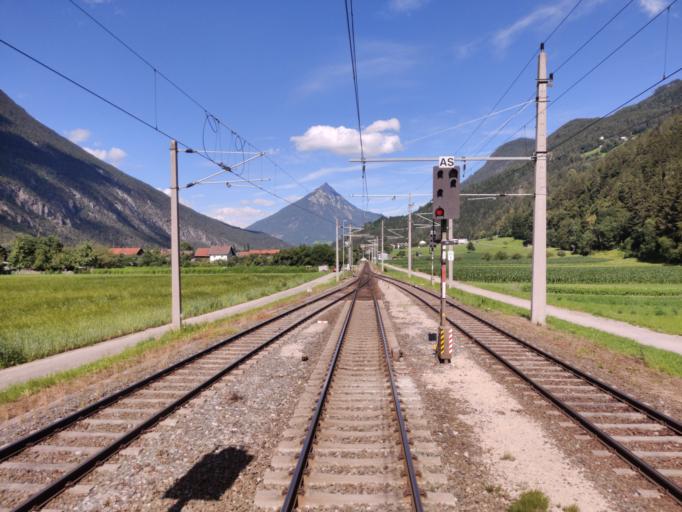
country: AT
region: Tyrol
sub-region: Politischer Bezirk Landeck
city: Schonwies
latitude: 47.1985
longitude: 10.6654
